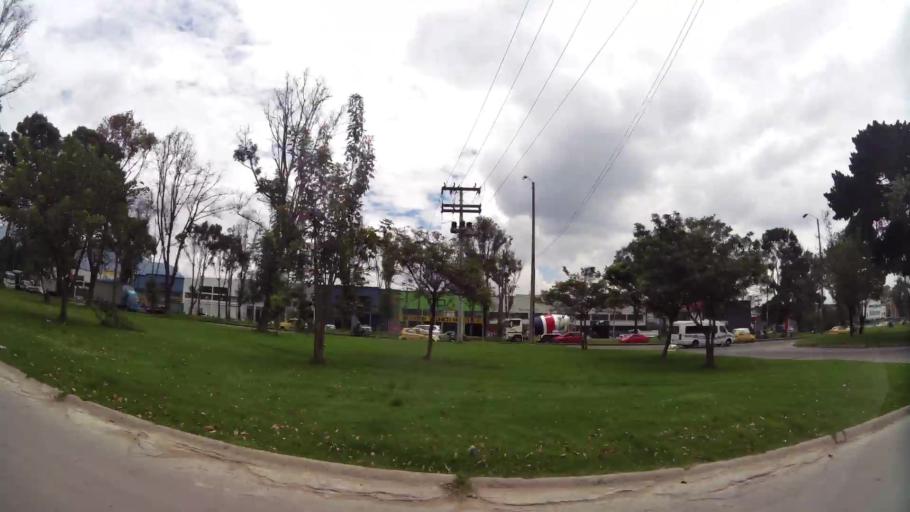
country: CO
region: Bogota D.C.
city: Bogota
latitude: 4.6262
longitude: -74.0928
